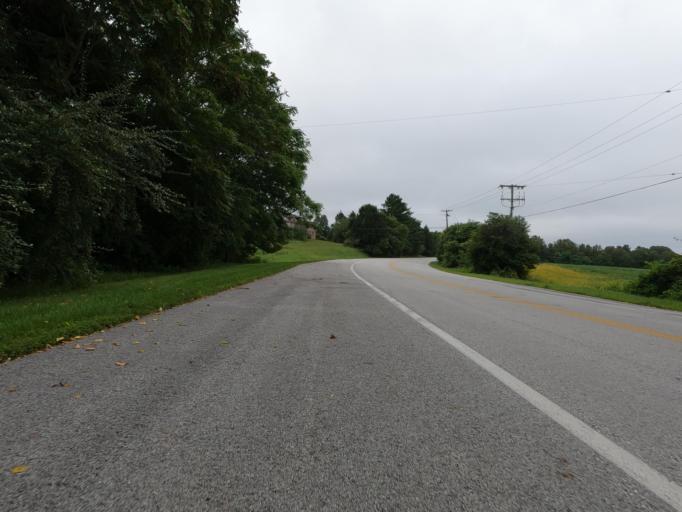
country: US
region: Maryland
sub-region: Carroll County
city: Sykesville
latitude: 39.3408
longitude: -77.0488
